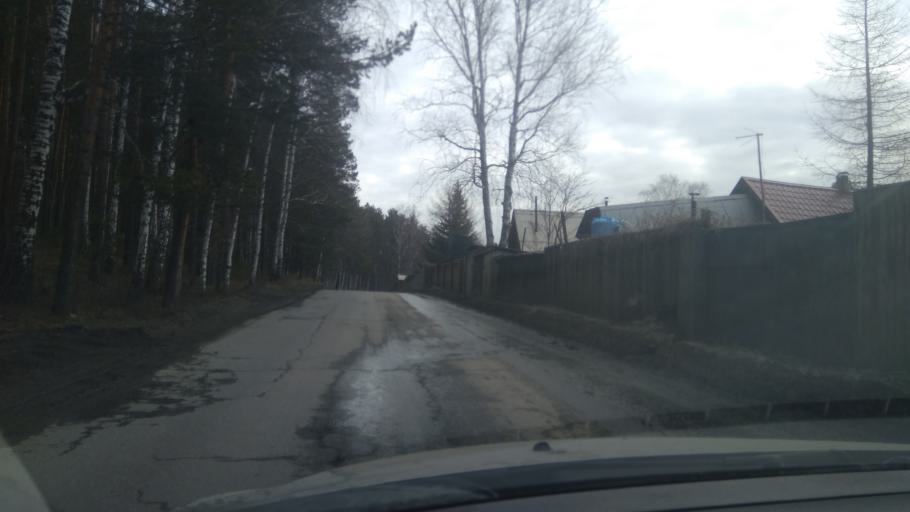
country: RU
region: Sverdlovsk
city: Severka
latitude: 56.8433
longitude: 60.3841
